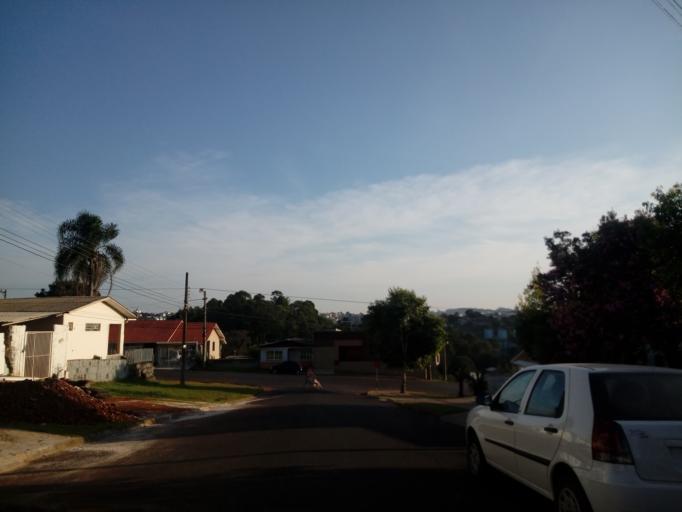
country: BR
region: Santa Catarina
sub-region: Chapeco
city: Chapeco
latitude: -27.0898
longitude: -52.6073
